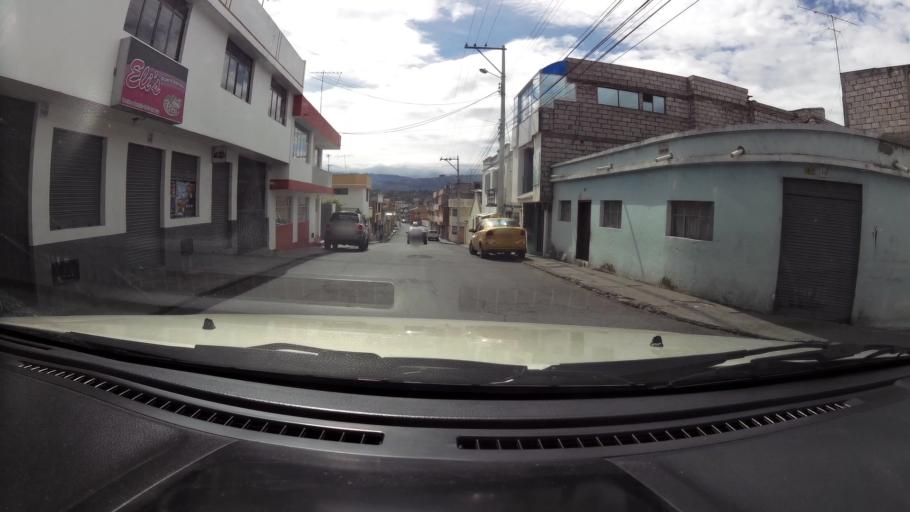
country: EC
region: Cotopaxi
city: Latacunga
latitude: -0.9241
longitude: -78.6206
